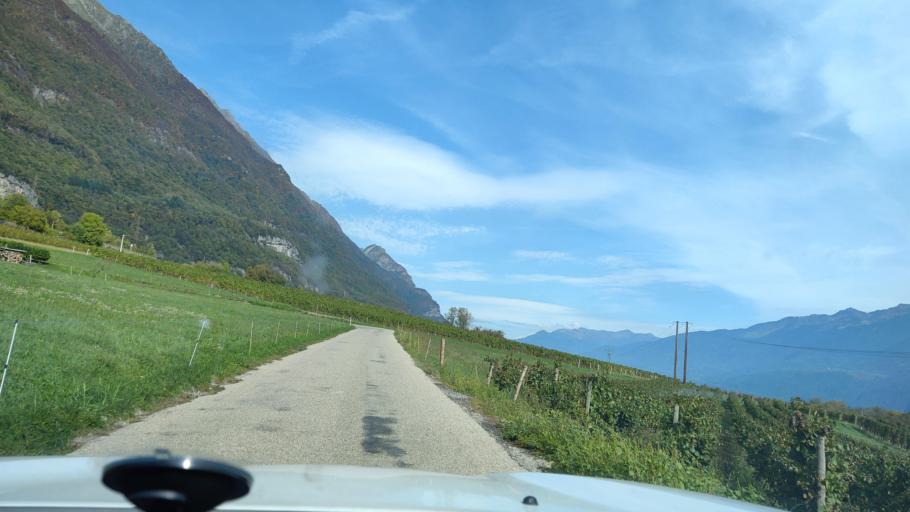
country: FR
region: Rhone-Alpes
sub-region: Departement de la Savoie
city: Coise-Saint-Jean-Pied-Gauthier
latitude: 45.5749
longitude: 6.1902
